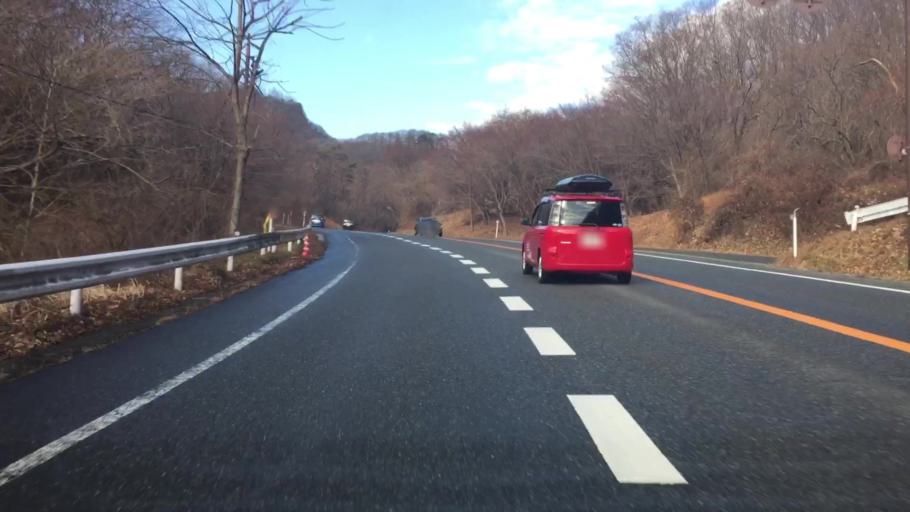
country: JP
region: Nagano
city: Saku
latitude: 36.3028
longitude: 138.6707
